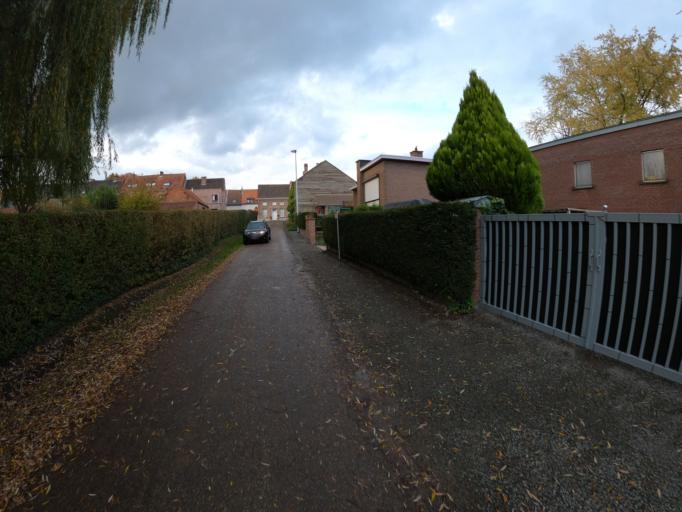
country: BE
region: Flanders
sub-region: Provincie Oost-Vlaanderen
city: Temse
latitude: 51.1153
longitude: 4.1863
